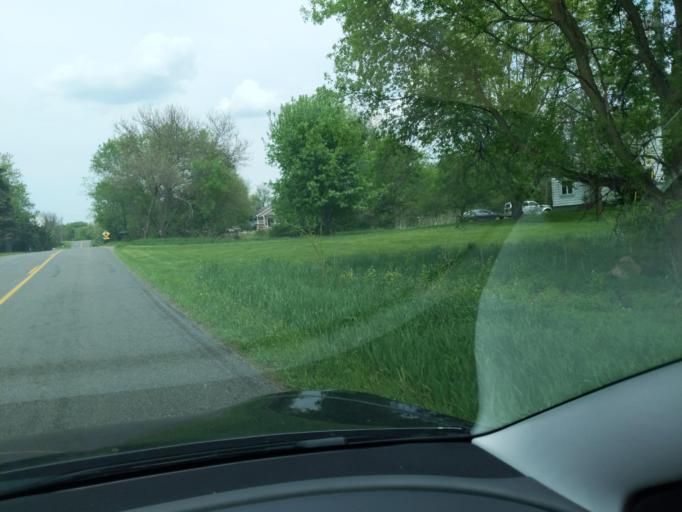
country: US
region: Michigan
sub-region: Ingham County
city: Stockbridge
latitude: 42.4514
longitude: -84.2246
